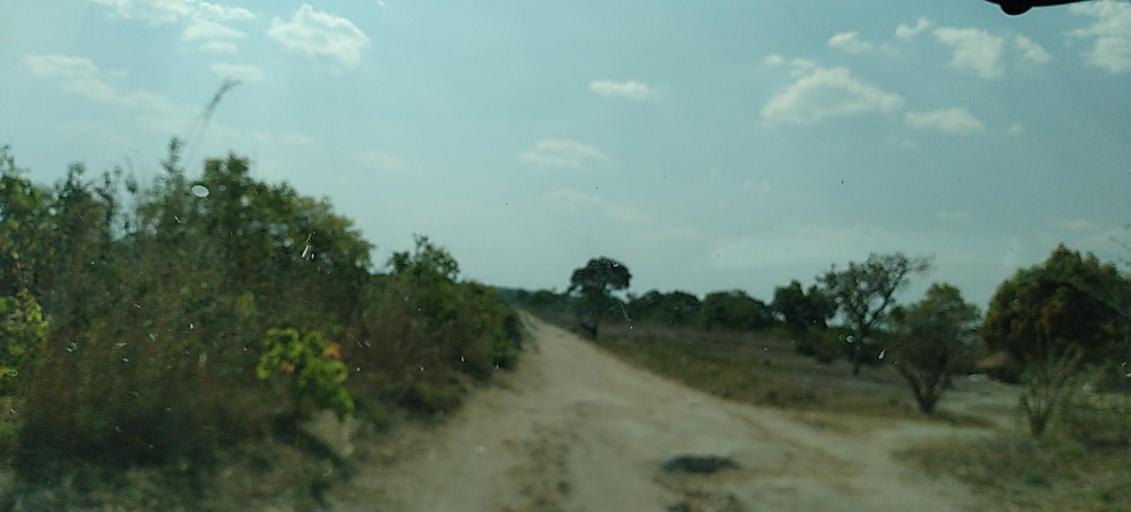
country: ZM
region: North-Western
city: Kalengwa
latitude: -13.1198
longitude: 25.0012
